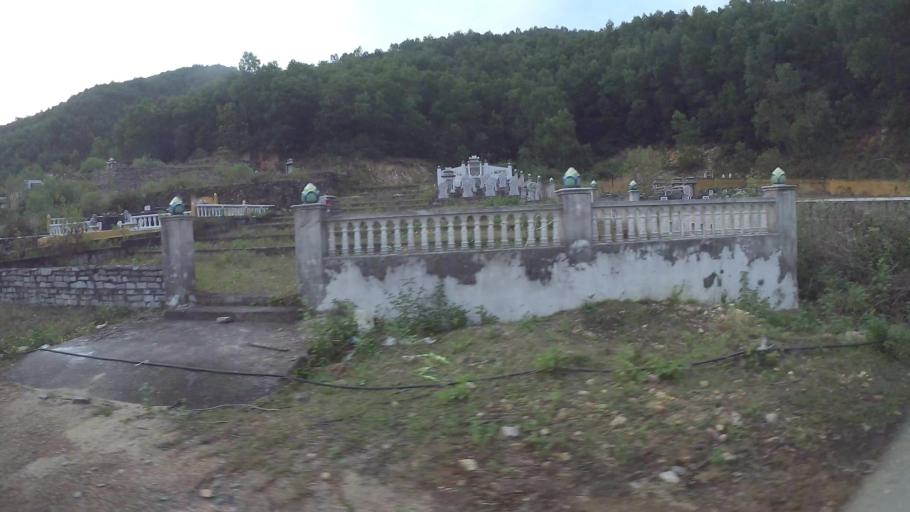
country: VN
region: Da Nang
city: Lien Chieu
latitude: 16.0624
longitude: 108.1200
